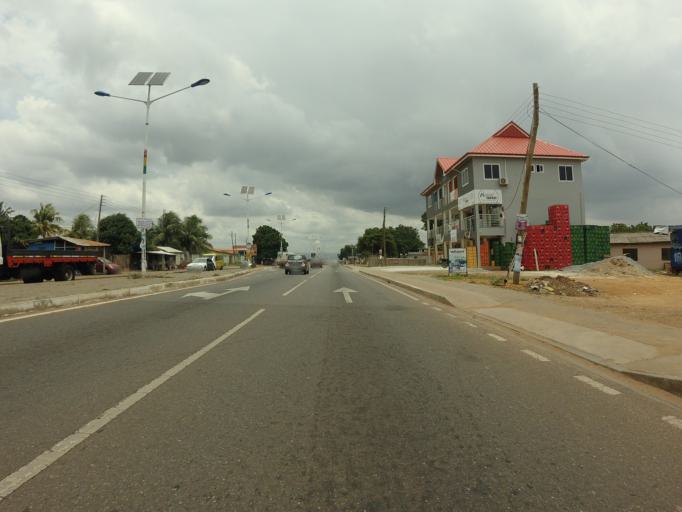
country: GH
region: Greater Accra
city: Medina Estates
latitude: 5.6663
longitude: -0.1515
